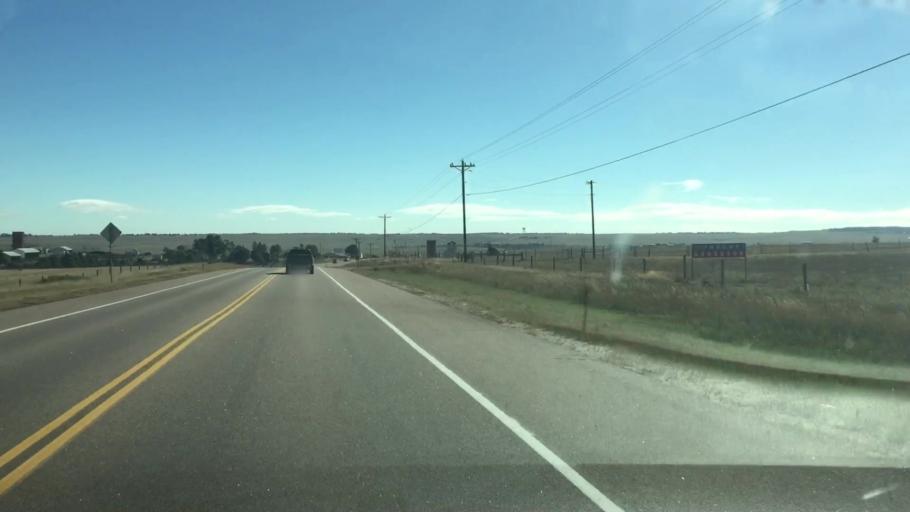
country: US
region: Colorado
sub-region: Elbert County
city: Kiowa
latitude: 39.3540
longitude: -104.5103
